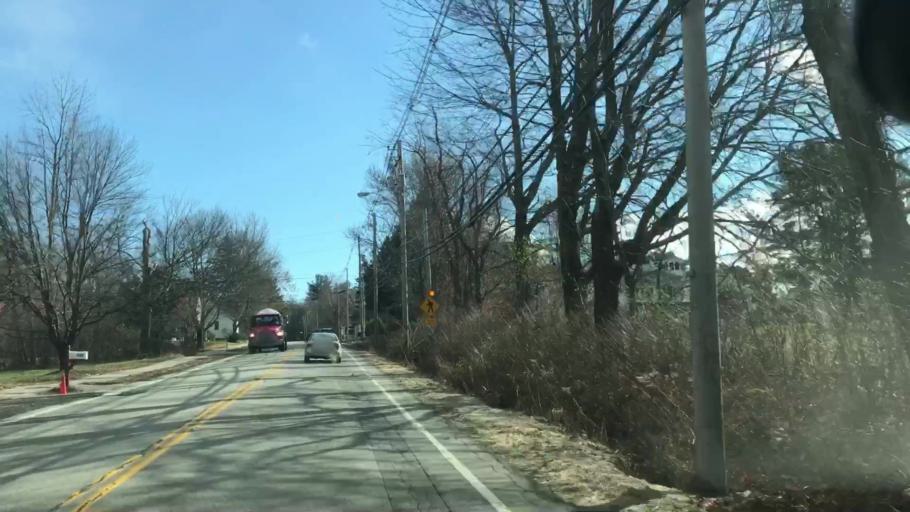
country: US
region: New Hampshire
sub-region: Carroll County
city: Wolfeboro
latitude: 43.5775
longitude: -71.1955
